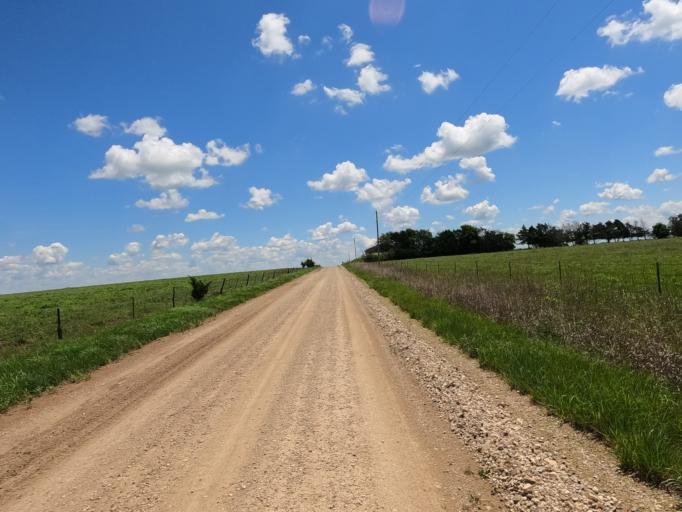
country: US
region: Kansas
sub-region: Chase County
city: Cottonwood Falls
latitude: 38.2169
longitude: -96.7354
